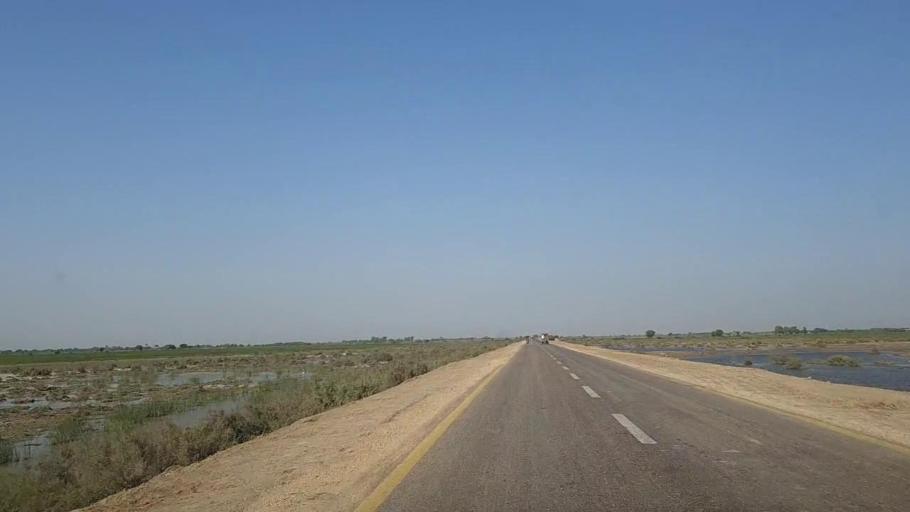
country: PK
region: Sindh
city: Jati
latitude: 24.4004
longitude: 68.2934
